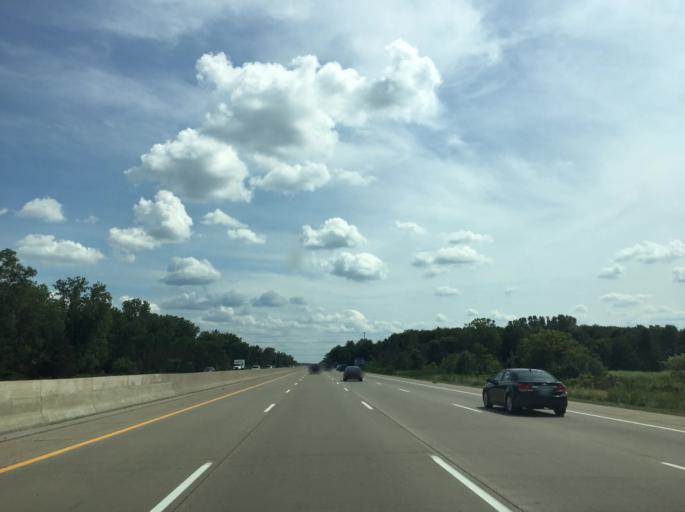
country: US
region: Michigan
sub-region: Genesee County
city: Clio
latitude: 43.2044
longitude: -83.7692
